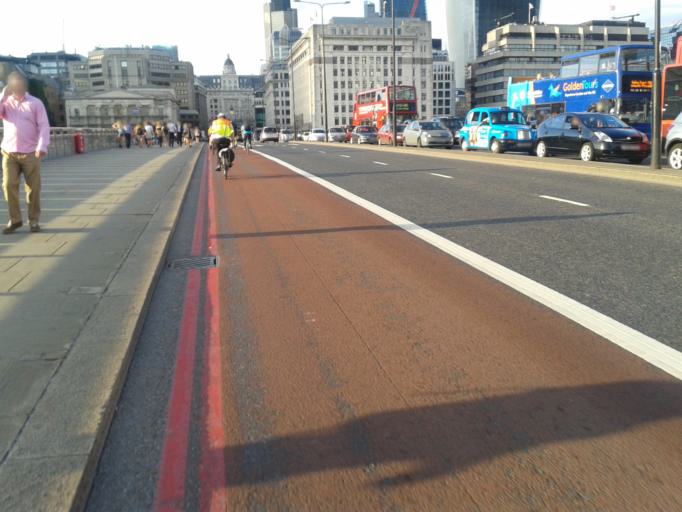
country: GB
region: England
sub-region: Greater London
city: City of London
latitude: 51.5073
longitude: -0.0880
